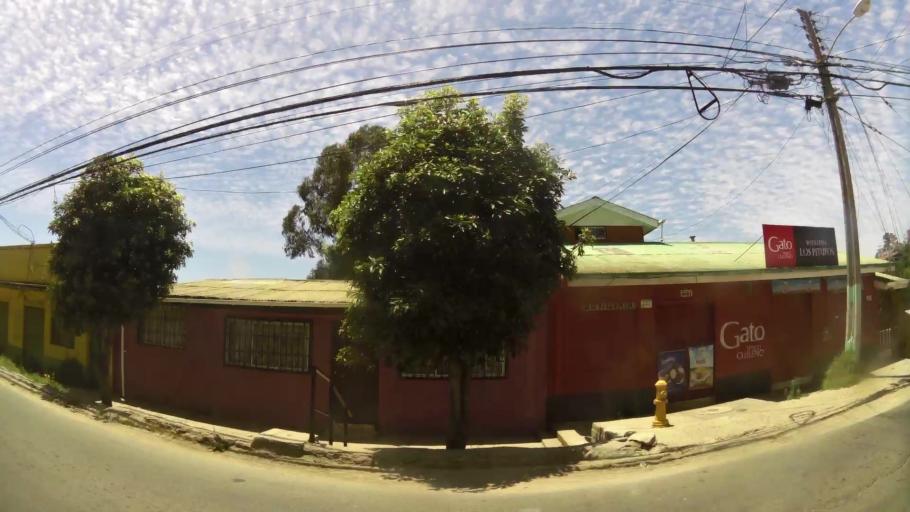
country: CL
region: Valparaiso
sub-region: Provincia de Valparaiso
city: Valparaiso
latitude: -33.0435
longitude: -71.5876
